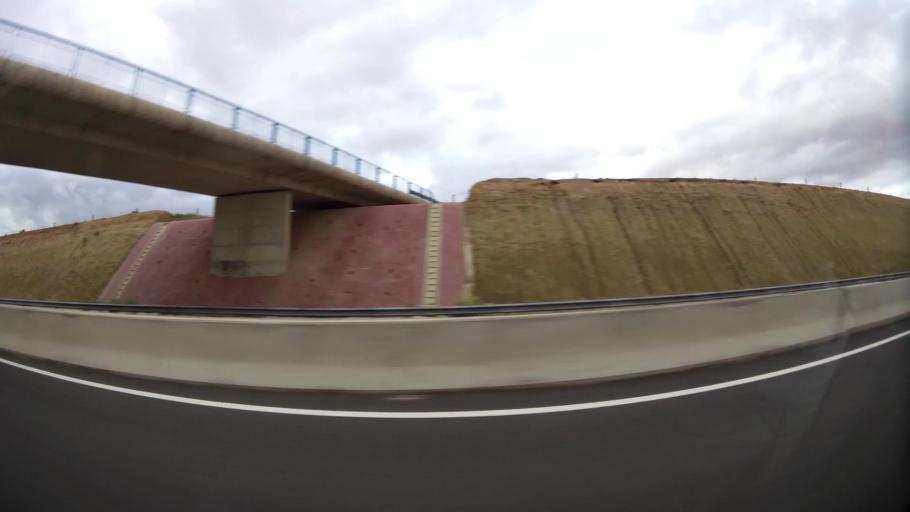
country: MA
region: Taza-Al Hoceima-Taounate
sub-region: Taza
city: Guercif
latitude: 34.3045
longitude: -3.6598
